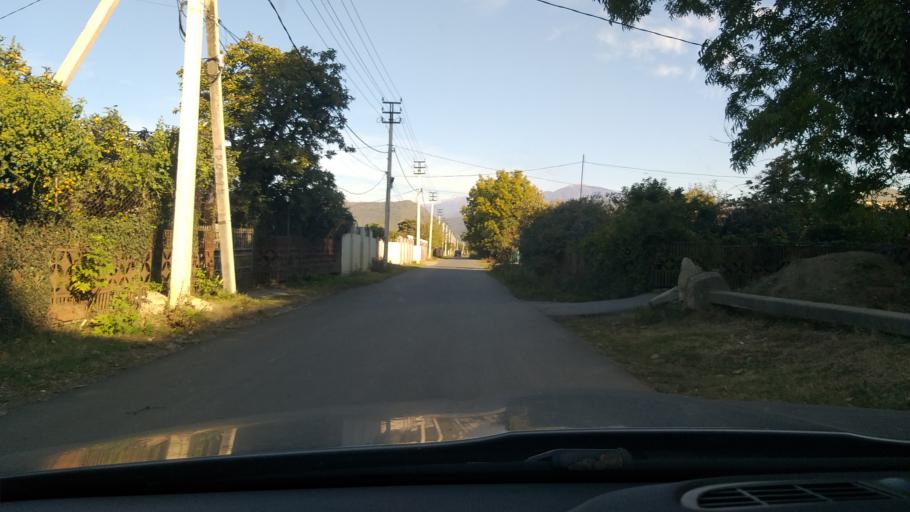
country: GE
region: Abkhazia
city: Sokhumi
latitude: 43.0148
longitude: 40.9635
